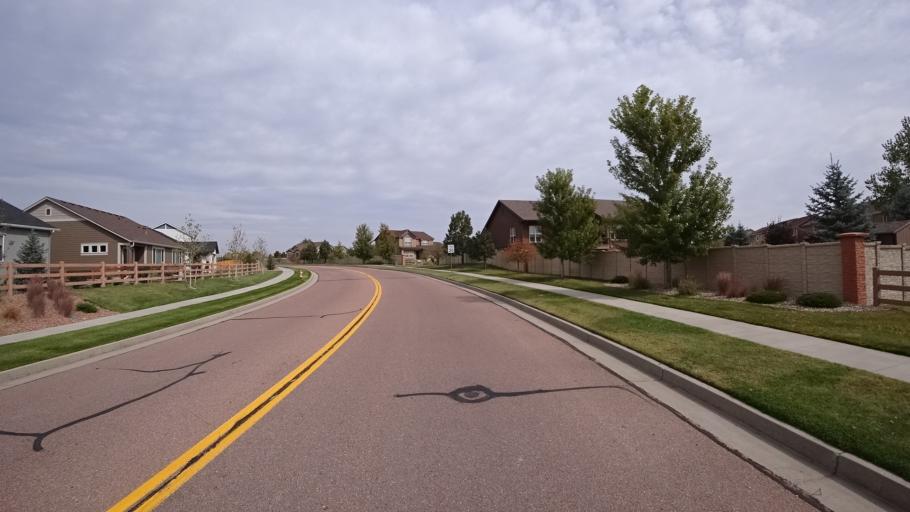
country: US
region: Colorado
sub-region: El Paso County
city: Cimarron Hills
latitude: 38.9176
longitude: -104.6865
